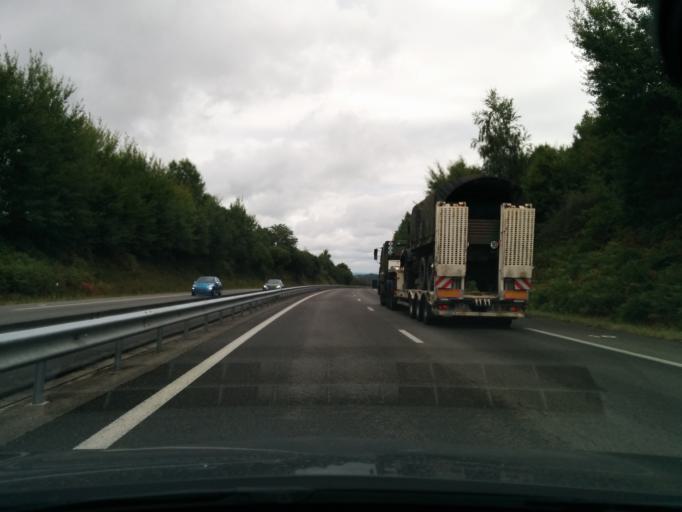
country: FR
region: Limousin
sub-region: Departement de la Haute-Vienne
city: Saint-Germain-les-Belles
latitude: 45.6023
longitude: 1.4470
